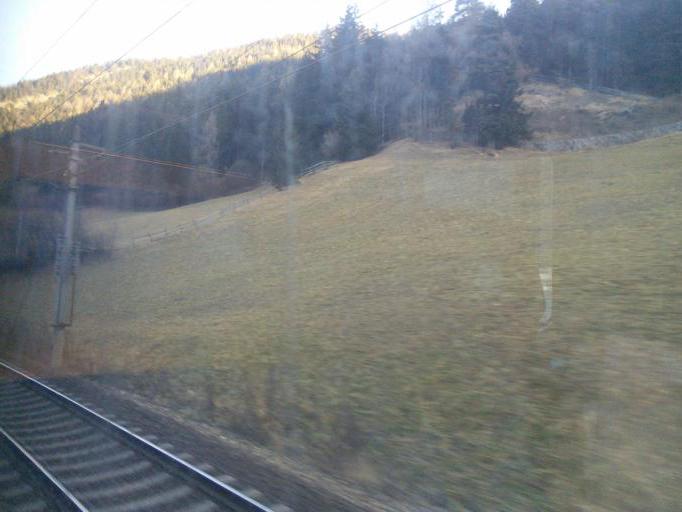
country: AT
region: Tyrol
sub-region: Politischer Bezirk Innsbruck Land
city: Gries am Brenner
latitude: 47.0702
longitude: 11.4866
